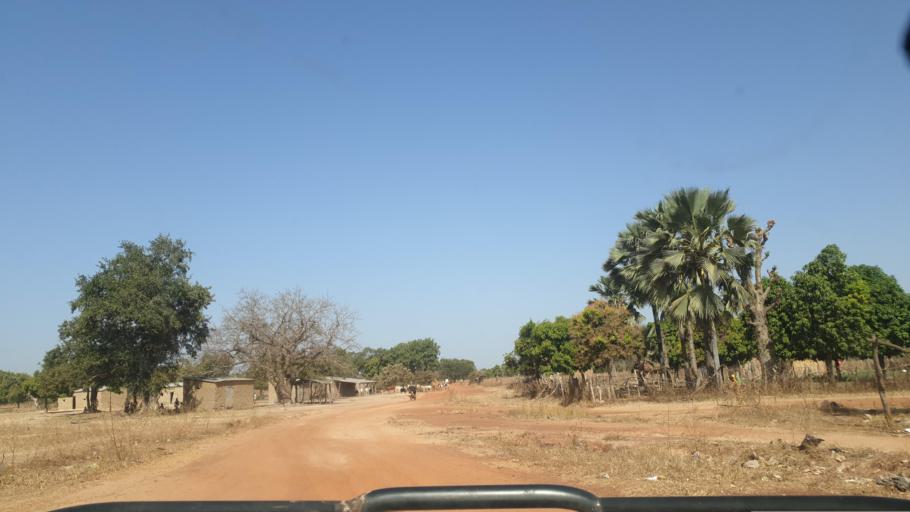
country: ML
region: Sikasso
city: Bougouni
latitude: 11.8142
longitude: -6.9360
